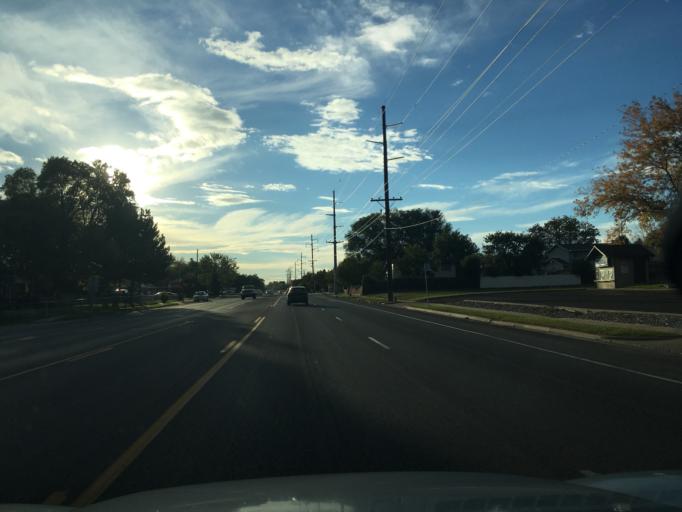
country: US
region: Utah
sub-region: Davis County
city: Layton
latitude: 41.0748
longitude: -111.9687
